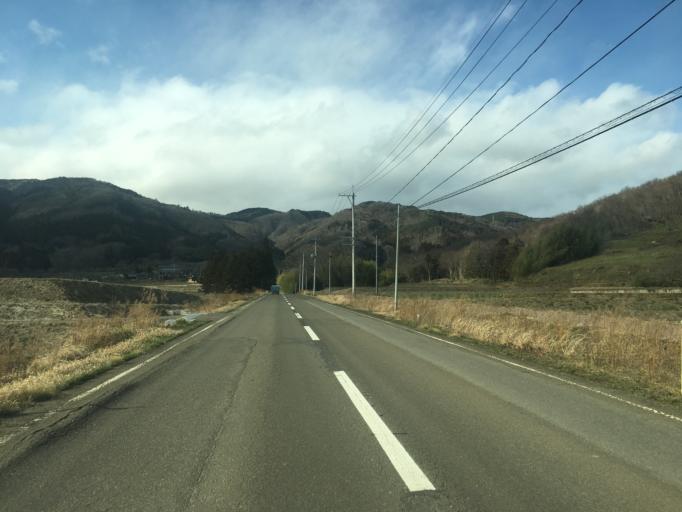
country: JP
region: Fukushima
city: Yanagawamachi-saiwaicho
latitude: 37.8974
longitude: 140.5801
